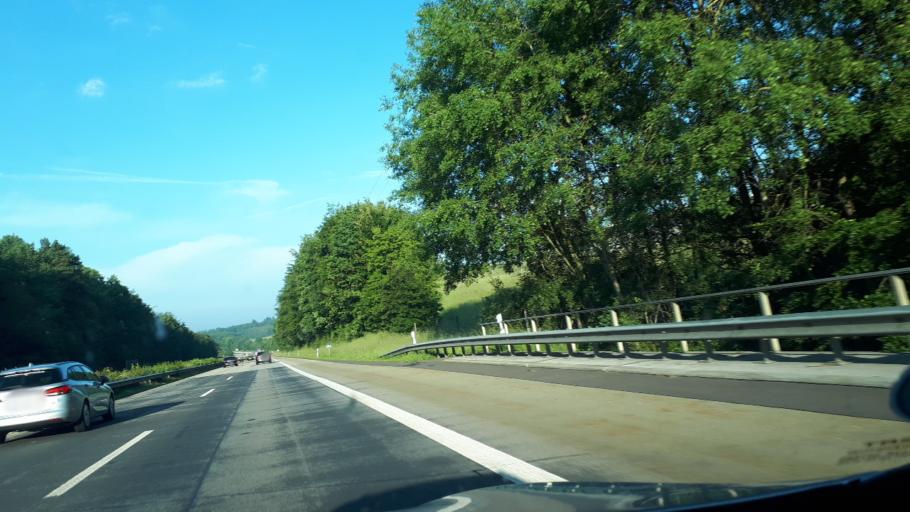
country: DE
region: Rheinland-Pfalz
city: Uersfeld
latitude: 50.2315
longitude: 7.0142
